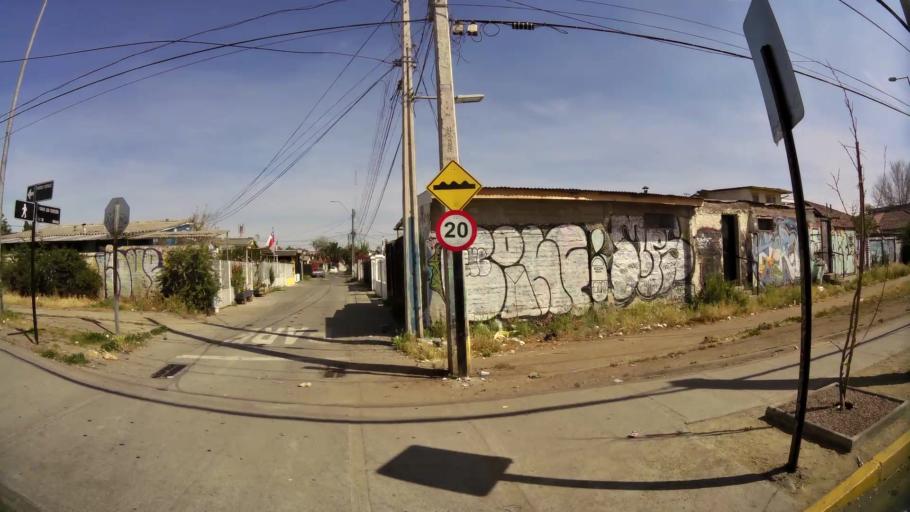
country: CL
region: Santiago Metropolitan
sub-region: Provincia de Santiago
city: La Pintana
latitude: -33.5371
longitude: -70.6659
